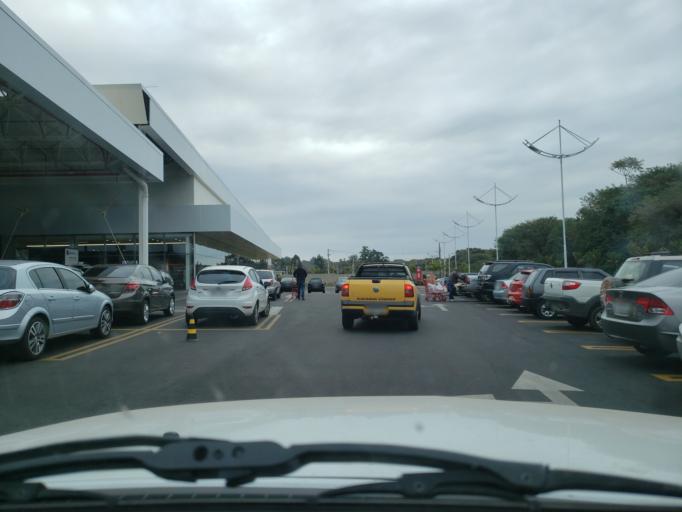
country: BR
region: Sao Paulo
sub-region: Moji-Guacu
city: Mogi-Gaucu
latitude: -22.3757
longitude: -46.9454
